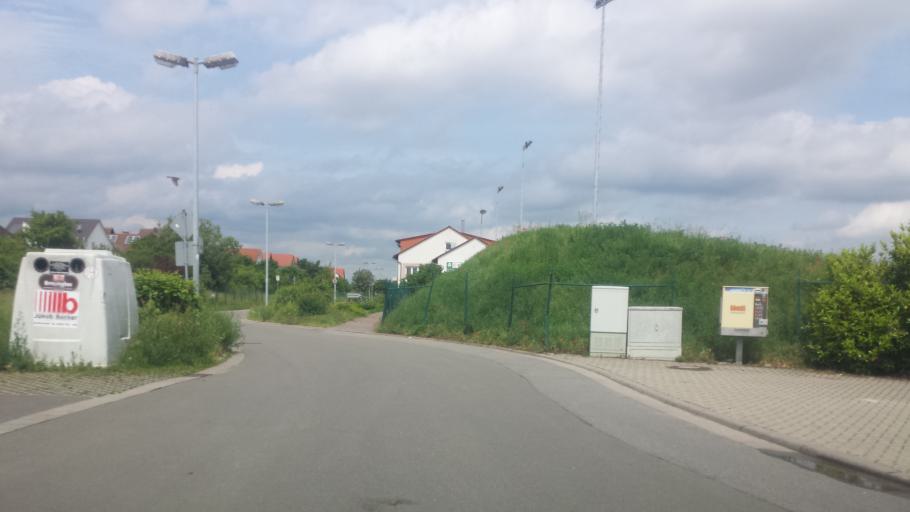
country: DE
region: Rheinland-Pfalz
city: Wachenheim
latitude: 49.4398
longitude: 8.1913
